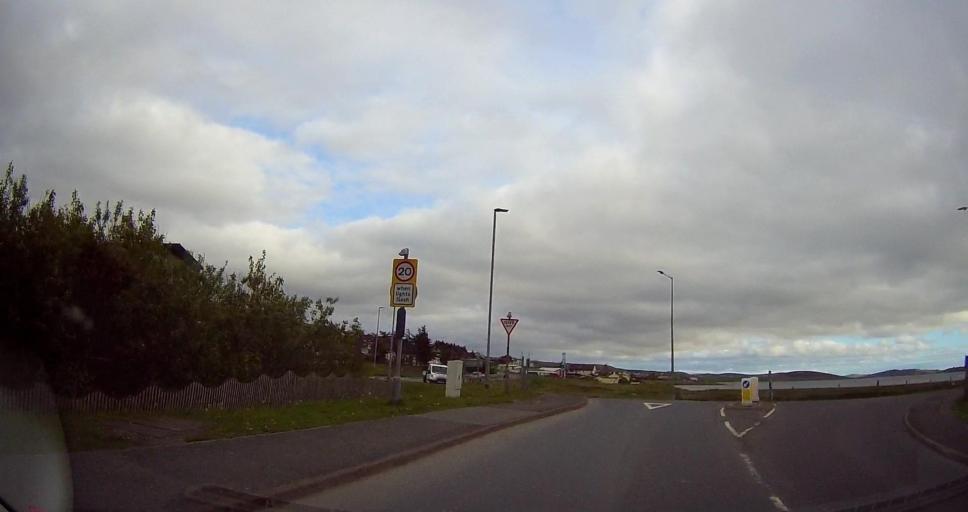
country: GB
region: Scotland
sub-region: Shetland Islands
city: Lerwick
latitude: 60.3968
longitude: -1.3542
